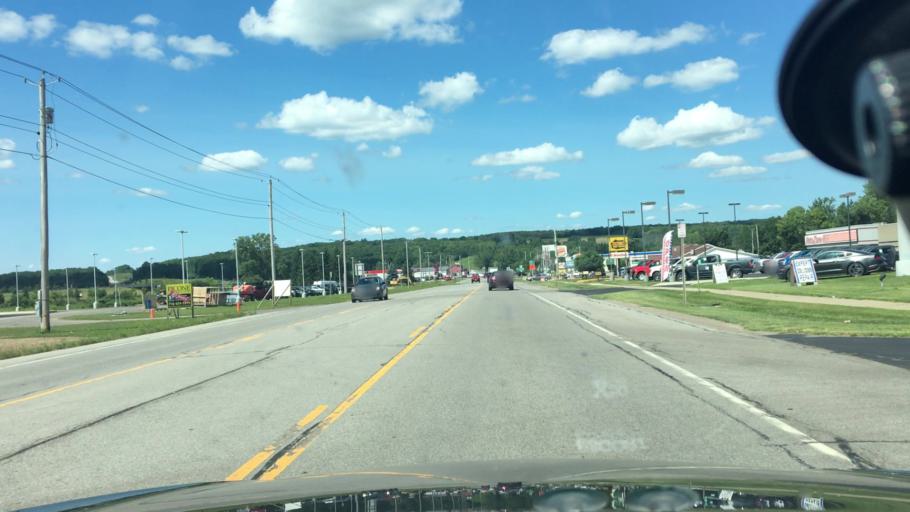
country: US
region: New York
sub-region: Erie County
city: Springville
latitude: 42.5054
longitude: -78.6894
